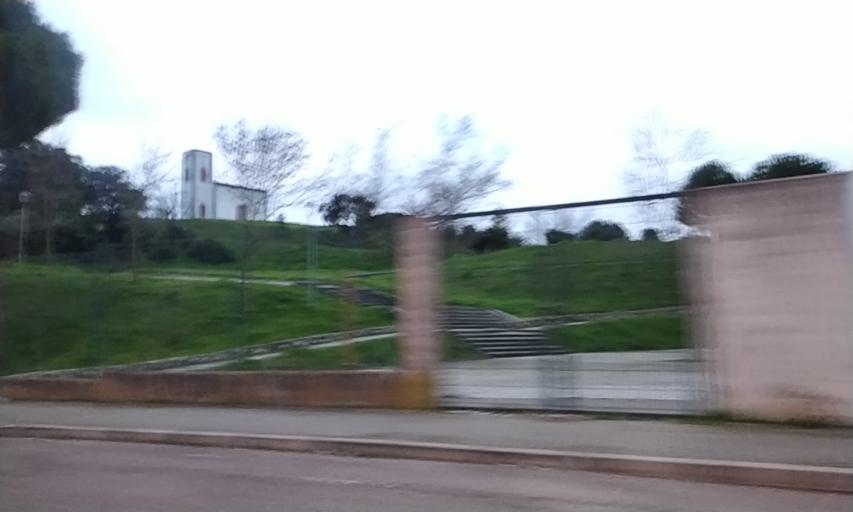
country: PT
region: Setubal
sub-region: Setubal
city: Setubal
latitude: 38.5187
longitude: -8.8630
